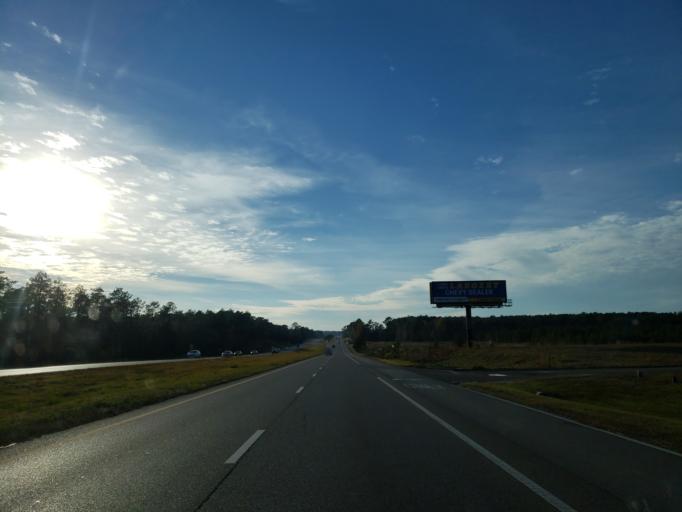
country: US
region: Mississippi
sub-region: Lamar County
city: West Hattiesburg
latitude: 31.3153
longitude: -89.4453
